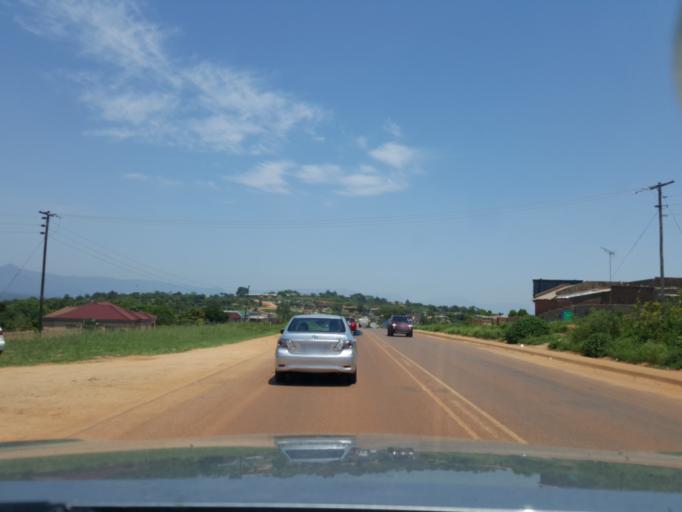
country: ZA
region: Limpopo
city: Thulamahashi
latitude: -24.8483
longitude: 31.1020
